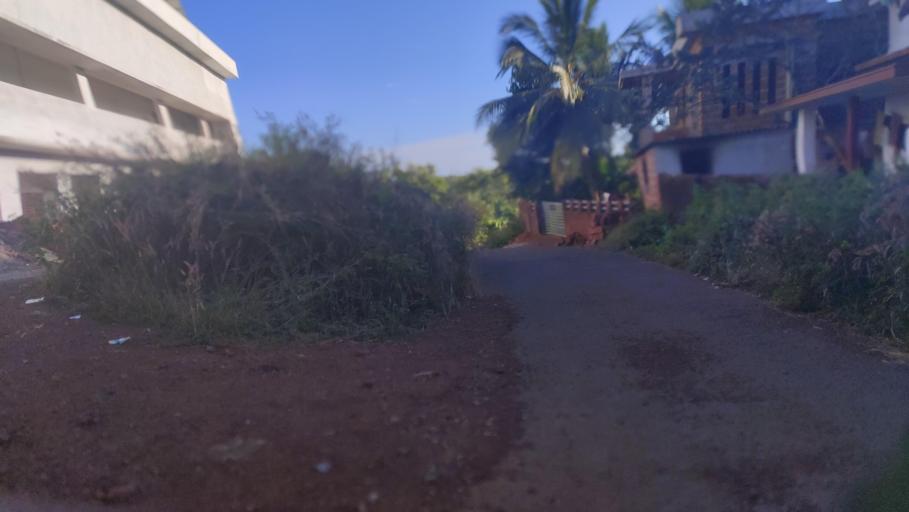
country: IN
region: Kerala
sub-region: Kasaragod District
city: Kasaragod
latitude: 12.5046
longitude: 75.0774
